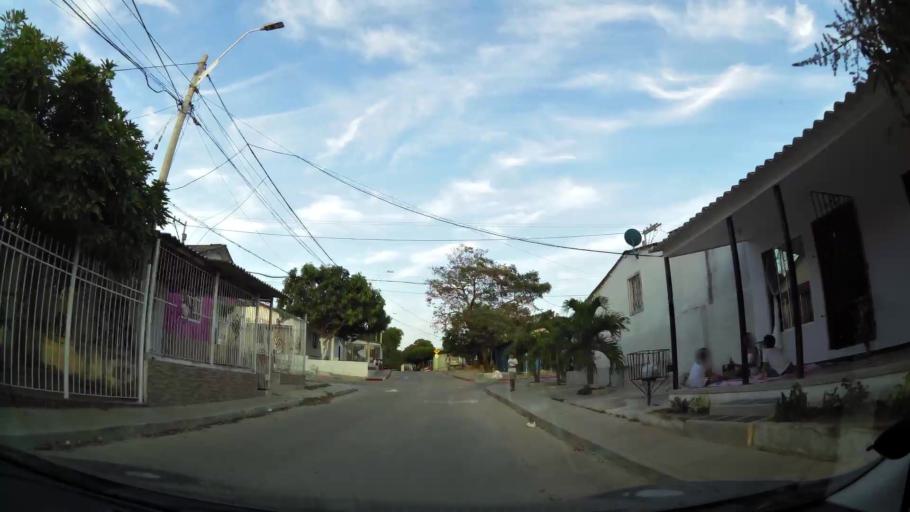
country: CO
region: Atlantico
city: Barranquilla
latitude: 10.9469
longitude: -74.8206
